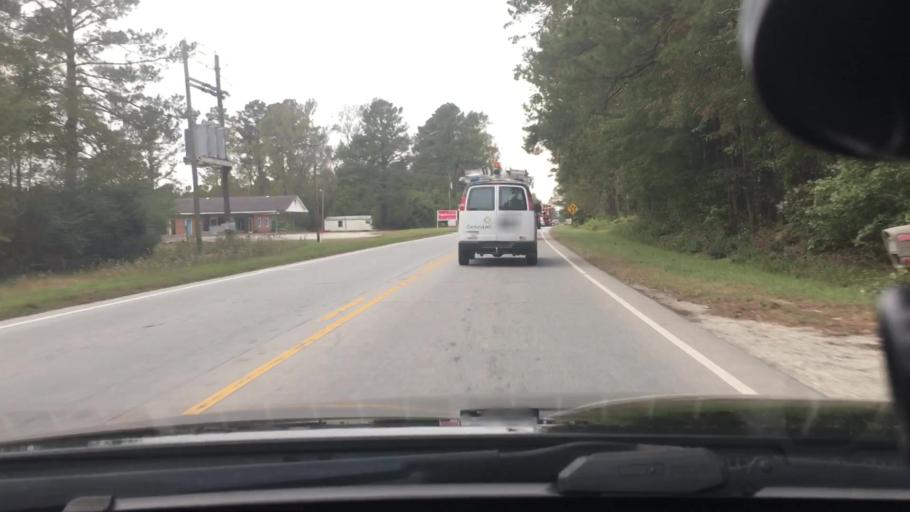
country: US
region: North Carolina
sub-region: Craven County
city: Vanceboro
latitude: 35.2796
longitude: -77.1216
